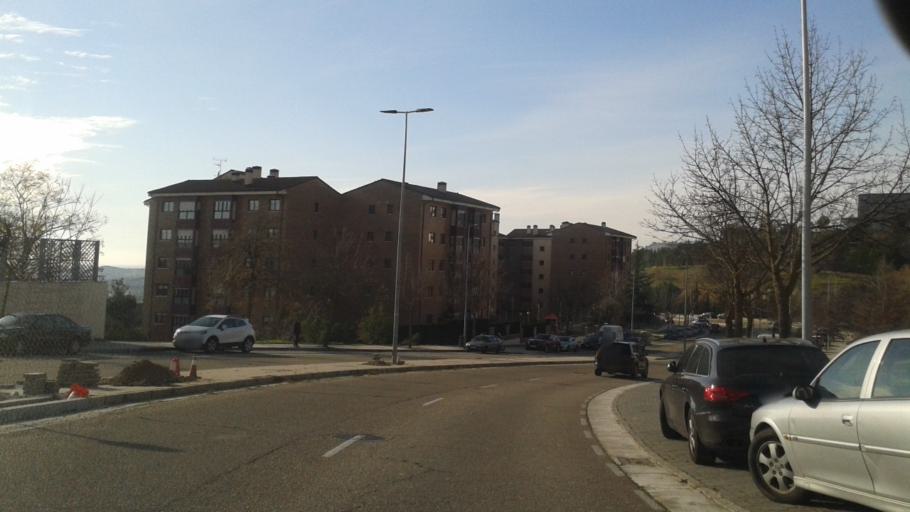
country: ES
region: Castille and Leon
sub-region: Provincia de Valladolid
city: Zaratan
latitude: 41.6348
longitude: -4.7624
